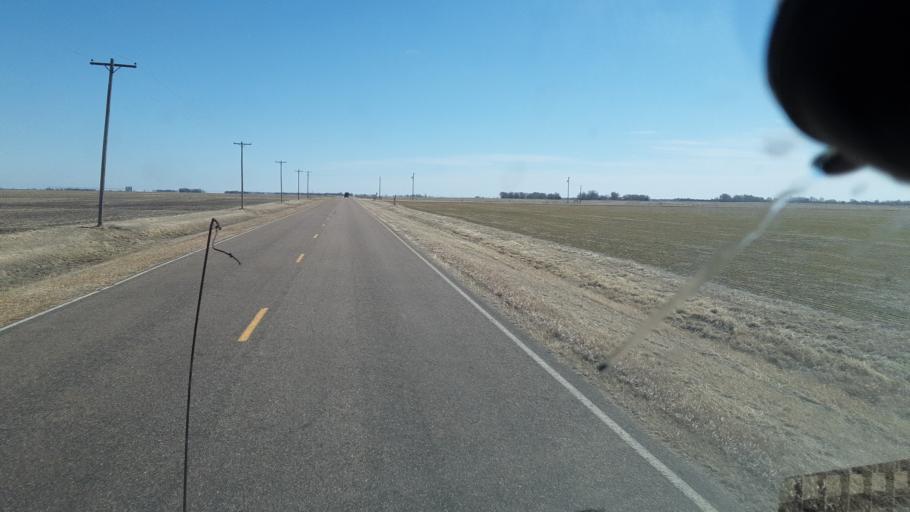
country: US
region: Kansas
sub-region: Rice County
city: Sterling
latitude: 38.2462
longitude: -98.2921
